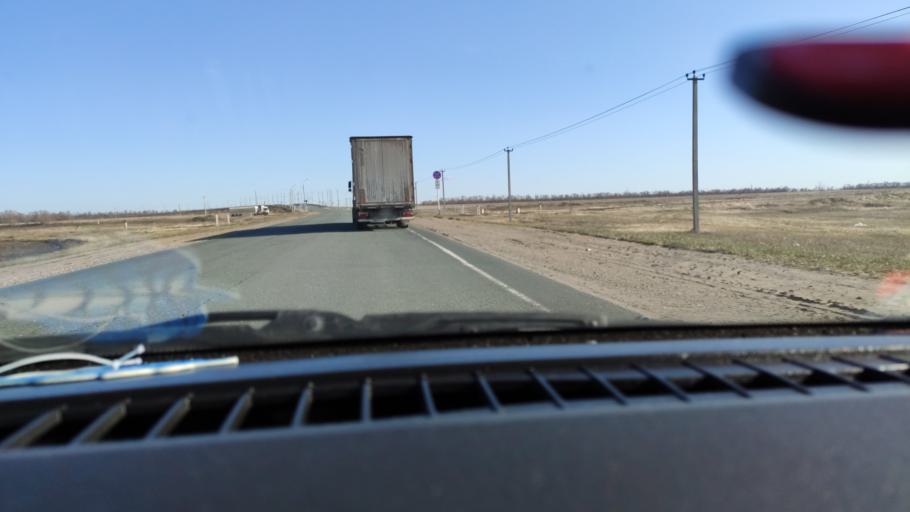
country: RU
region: Samara
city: Varlamovo
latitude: 53.1875
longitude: 48.2914
